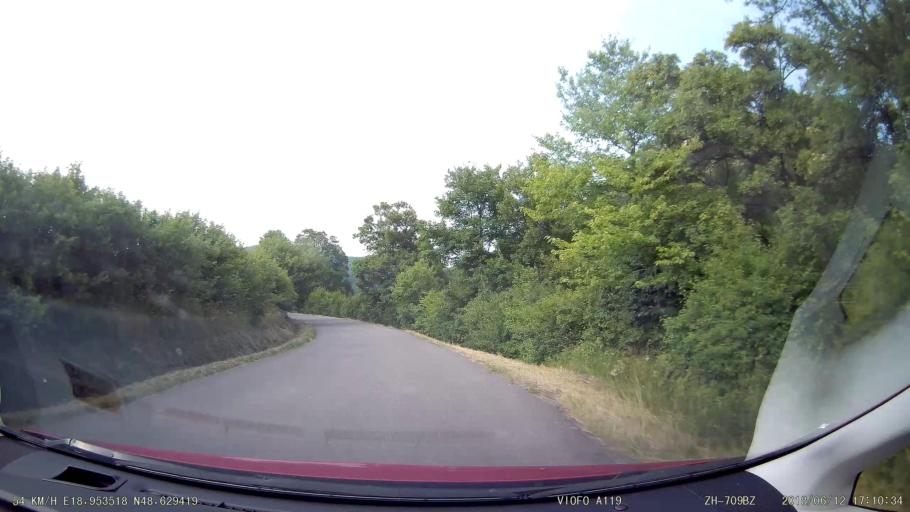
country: SK
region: Banskobystricky
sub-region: Okres Ziar nad Hronom
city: Kremnica
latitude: 48.6296
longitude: 18.9537
